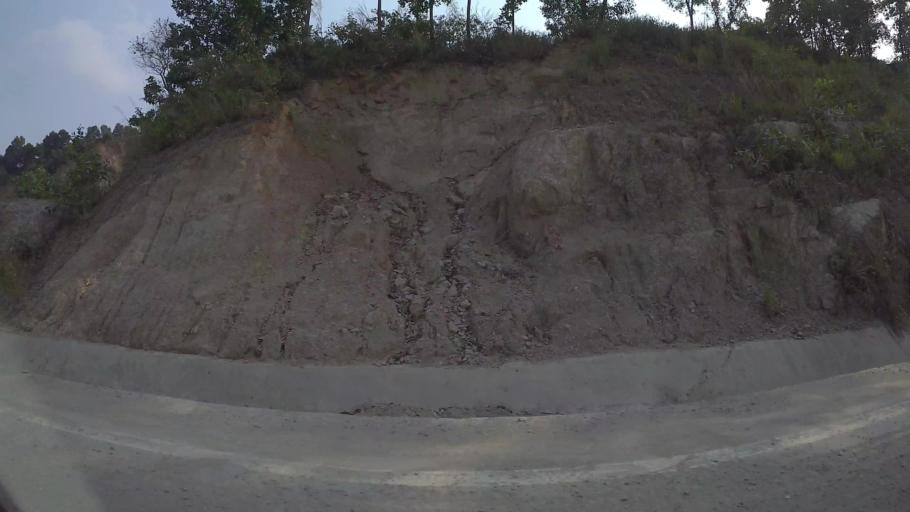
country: VN
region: Da Nang
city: Lien Chieu
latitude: 16.0419
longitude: 108.1643
